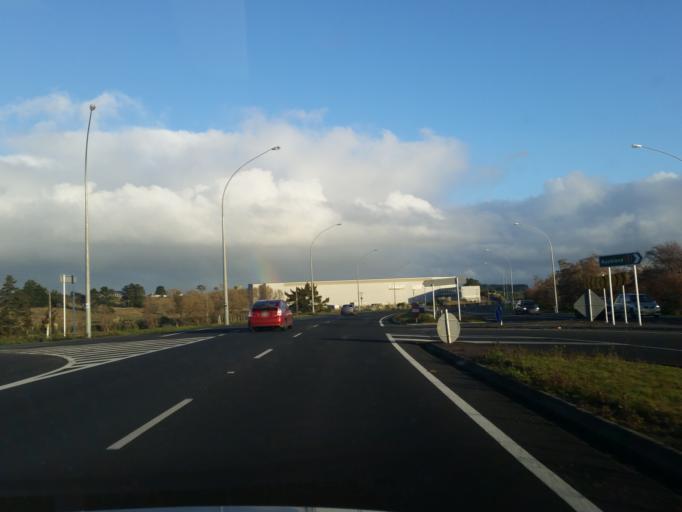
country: NZ
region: Waikato
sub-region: Waikato District
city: Te Kauwhata
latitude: -37.3089
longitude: 175.0674
